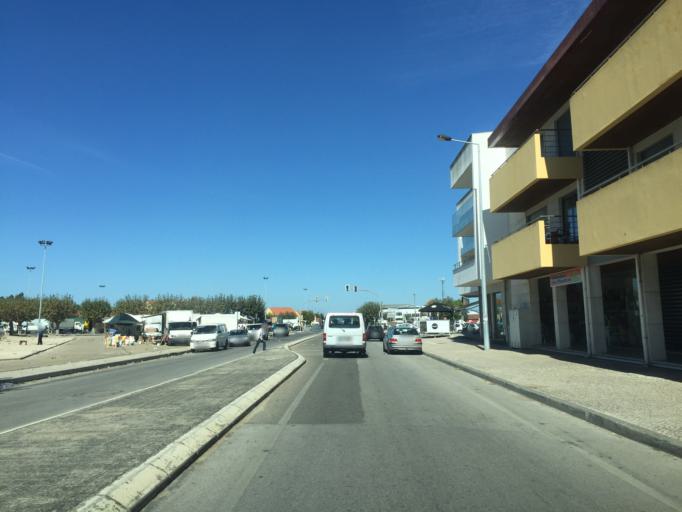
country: PT
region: Coimbra
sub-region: Montemor-O-Velho
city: Arazede
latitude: 40.3137
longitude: -8.7535
